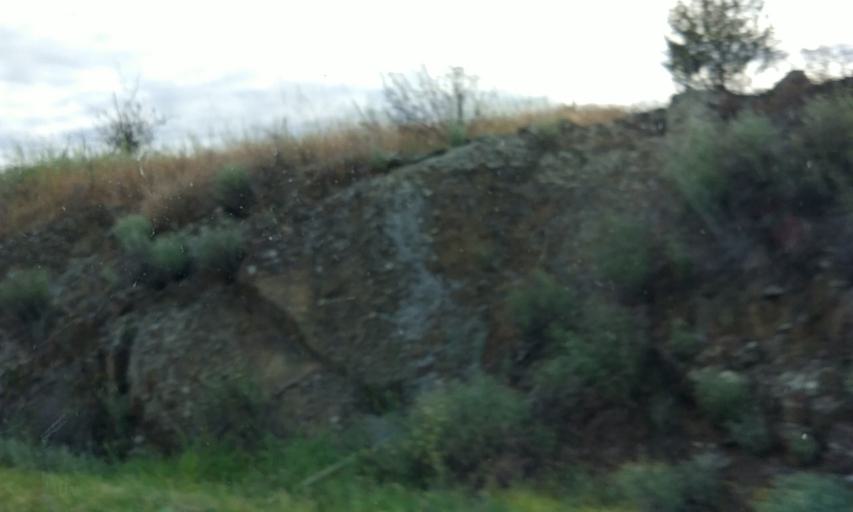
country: ES
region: Extremadura
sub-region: Provincia de Caceres
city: Coria
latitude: 39.9427
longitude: -6.5074
